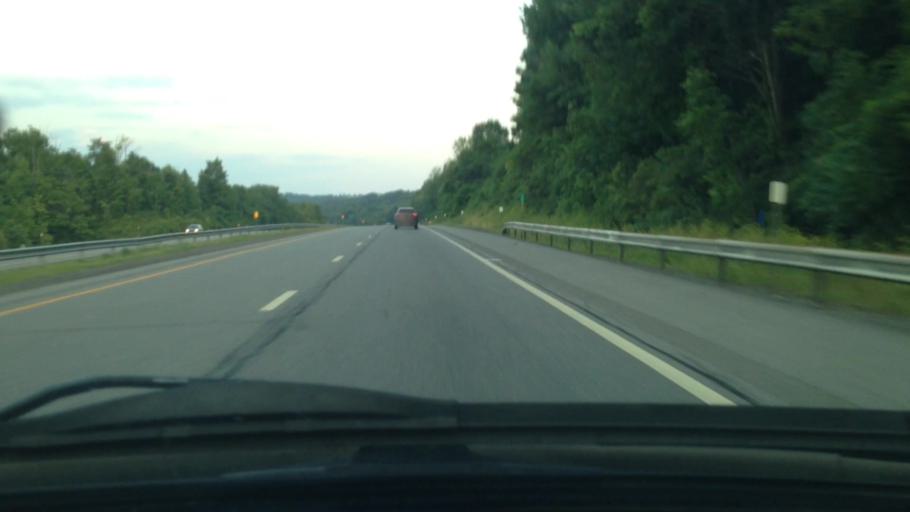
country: US
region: New York
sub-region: Montgomery County
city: Saint Johnsville
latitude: 42.9957
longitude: -74.7425
